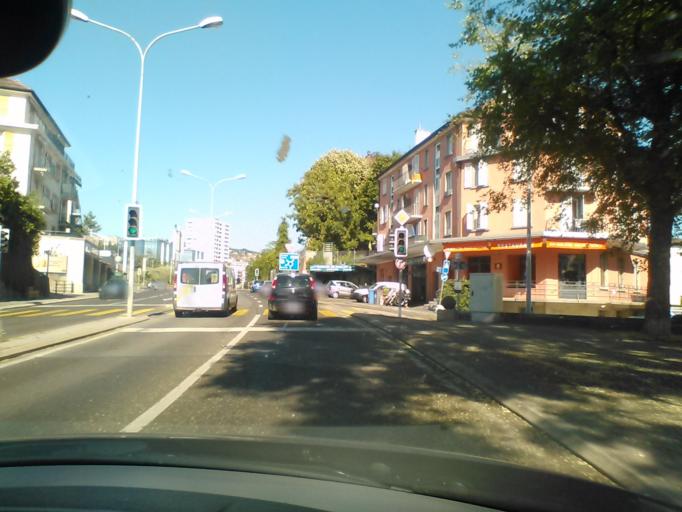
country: CH
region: Vaud
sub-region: Nyon District
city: Nyon
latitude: 46.3823
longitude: 6.2437
